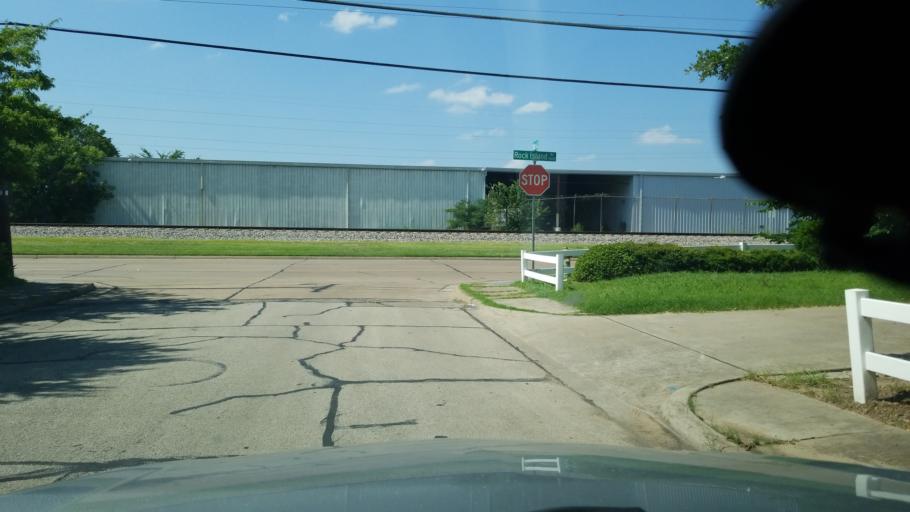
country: US
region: Texas
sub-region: Dallas County
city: Irving
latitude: 32.8148
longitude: -96.9653
